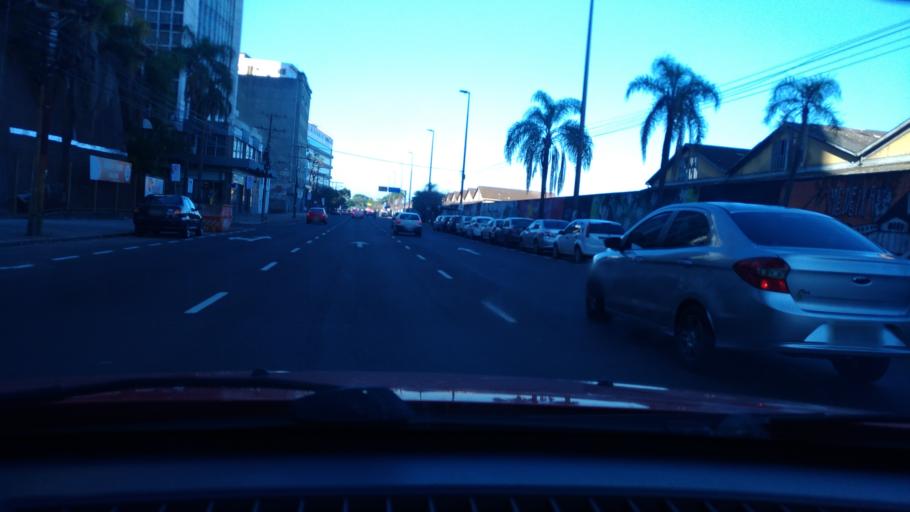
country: BR
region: Rio Grande do Sul
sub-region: Porto Alegre
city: Porto Alegre
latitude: -30.0288
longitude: -51.2339
